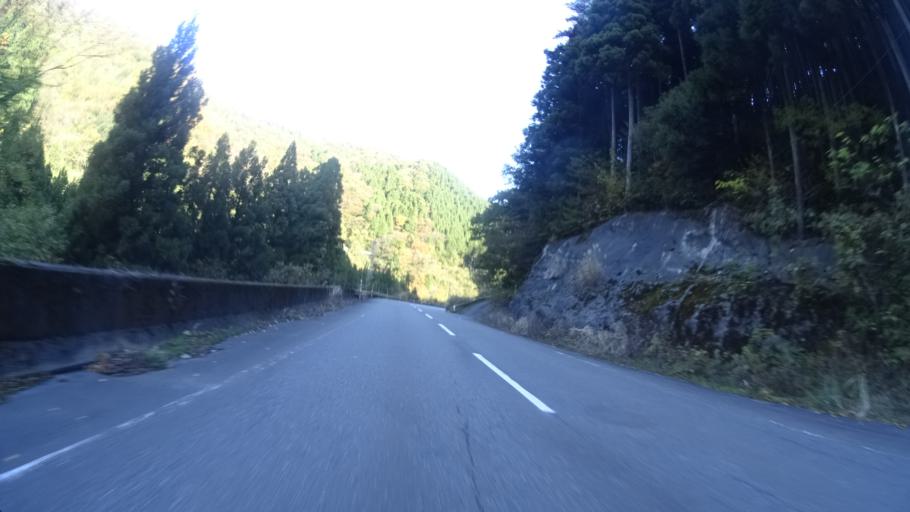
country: JP
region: Fukui
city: Maruoka
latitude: 36.2181
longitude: 136.3526
